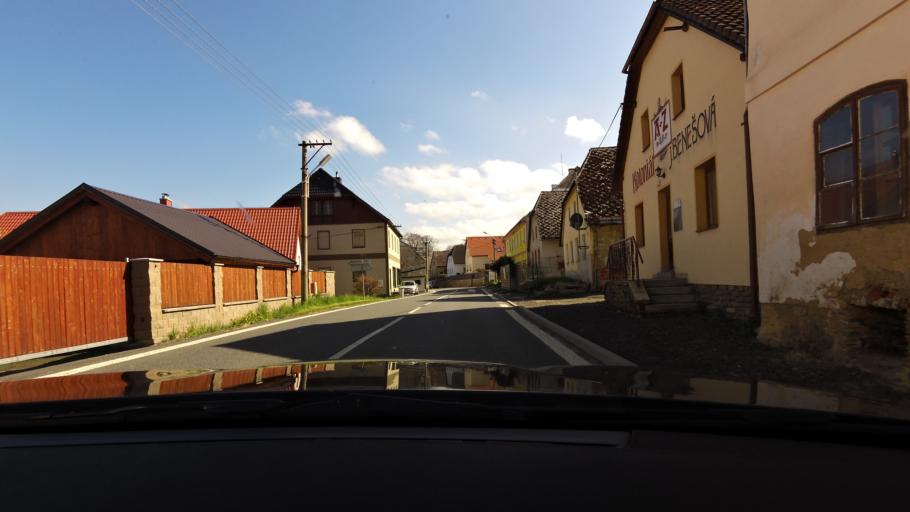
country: CZ
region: Plzensky
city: Strazov
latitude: 49.2662
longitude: 13.3027
